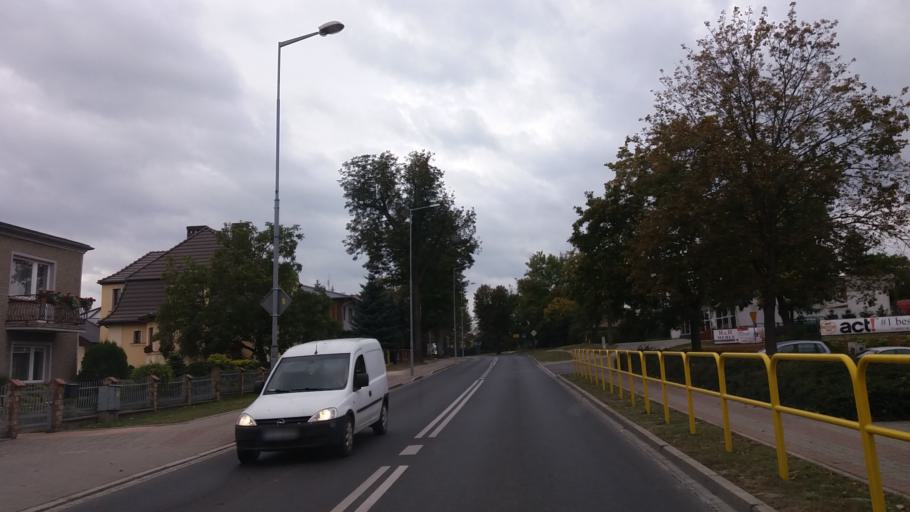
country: PL
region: Lubusz
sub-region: Powiat strzelecko-drezdenecki
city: Strzelce Krajenskie
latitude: 52.8742
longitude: 15.5244
